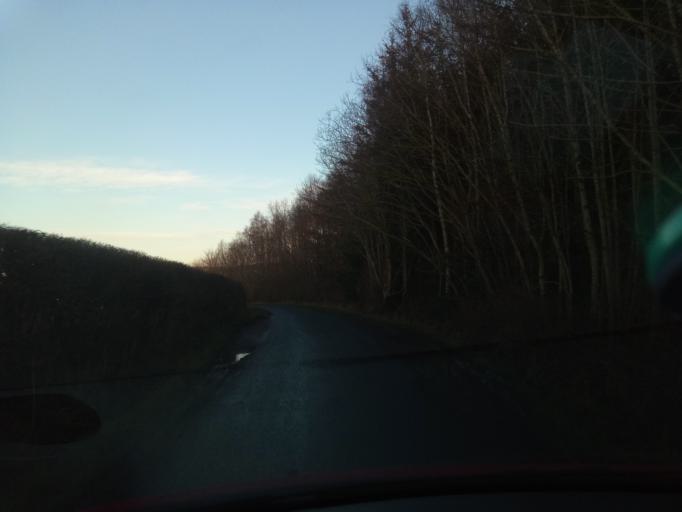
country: GB
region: Scotland
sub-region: The Scottish Borders
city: Melrose
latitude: 55.5894
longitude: -2.7366
